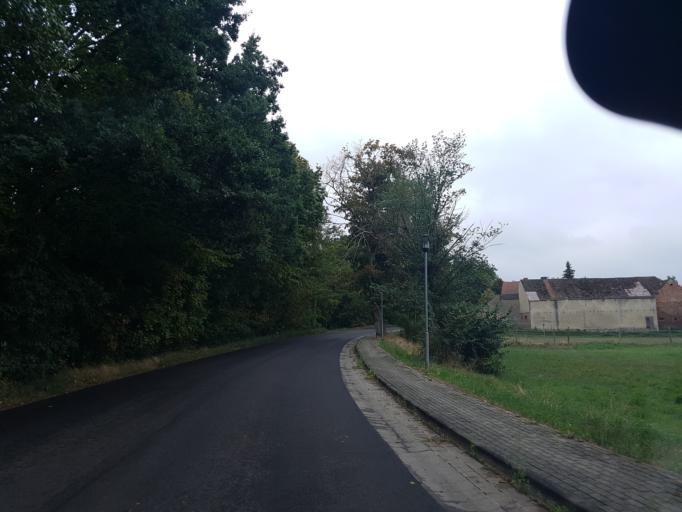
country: DE
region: Saxony-Anhalt
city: Loburg
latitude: 52.2307
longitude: 12.0732
